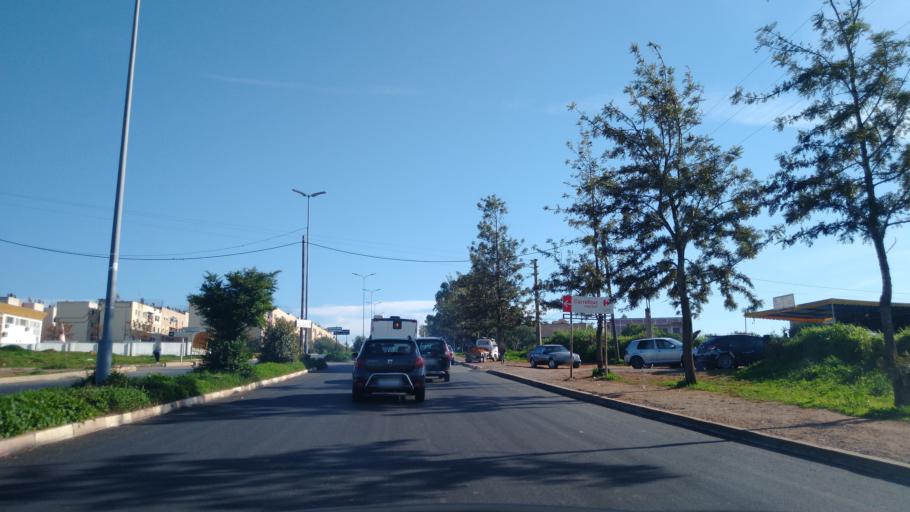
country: MA
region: Rabat-Sale-Zemmour-Zaer
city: Sale
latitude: 33.9997
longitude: -6.7504
